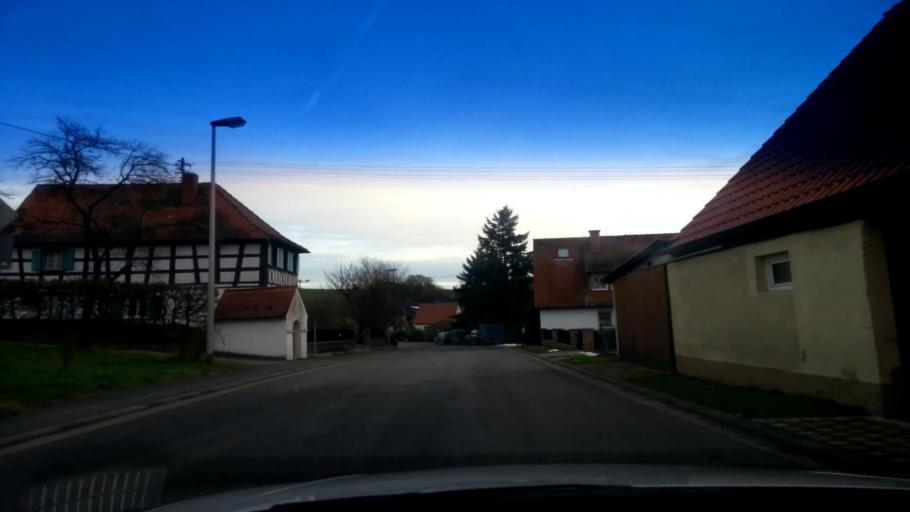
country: DE
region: Bavaria
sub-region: Upper Franconia
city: Strullendorf
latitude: 49.8675
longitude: 10.9984
